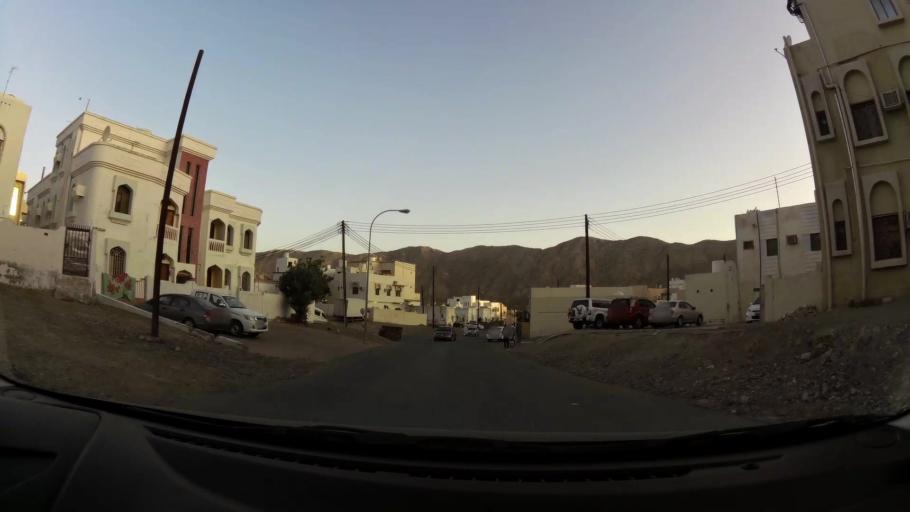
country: OM
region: Muhafazat Masqat
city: Muscat
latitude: 23.5785
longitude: 58.5714
